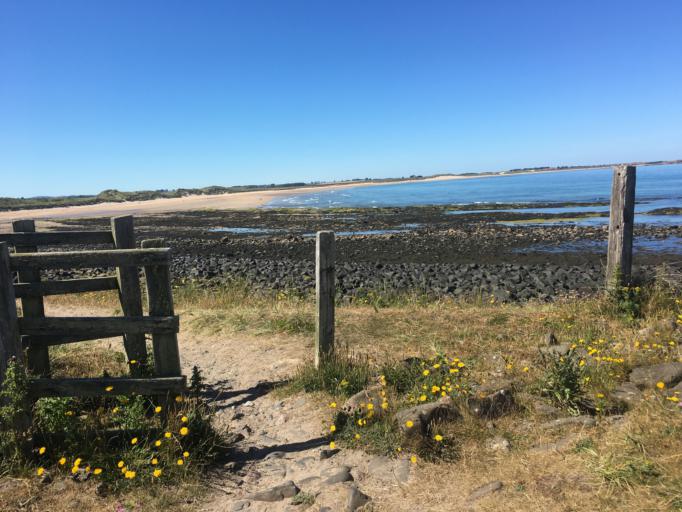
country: GB
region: England
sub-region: Northumberland
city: Beadnell
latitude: 55.5263
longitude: -1.6204
